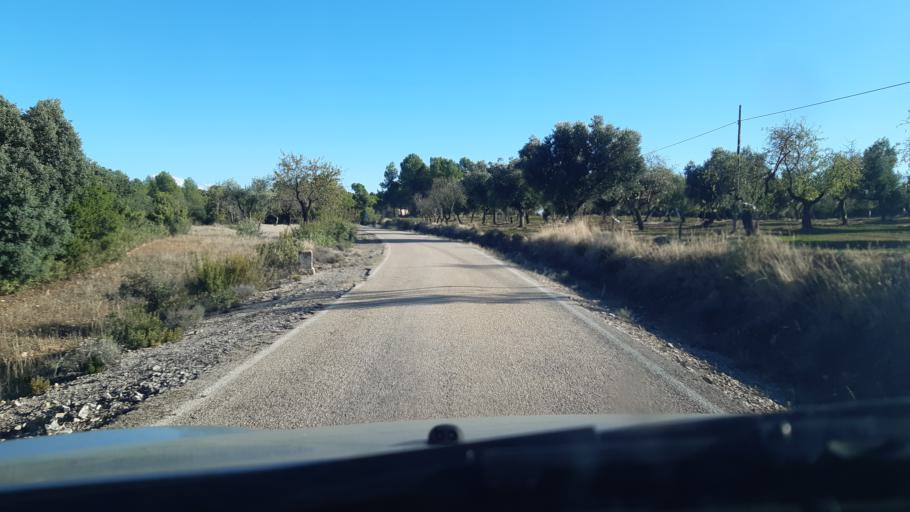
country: ES
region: Aragon
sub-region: Provincia de Teruel
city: Fornoles
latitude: 40.9133
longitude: -0.0192
